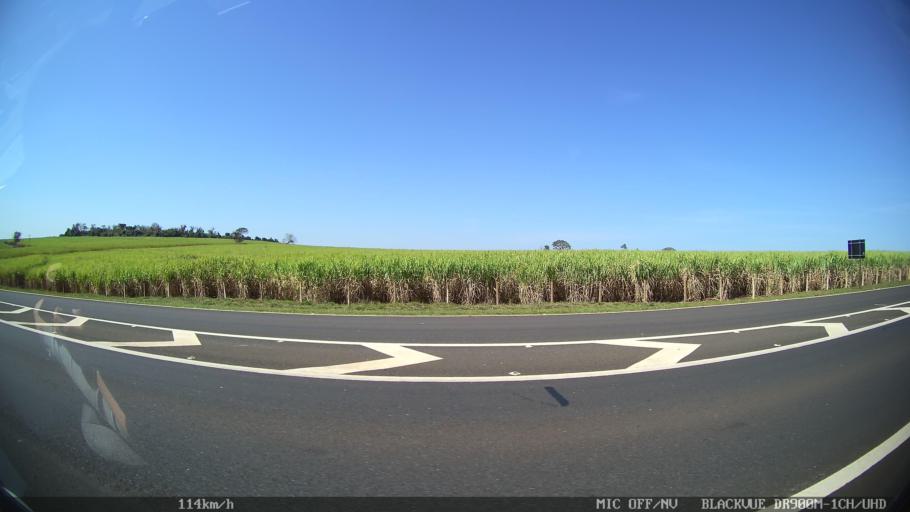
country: BR
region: Sao Paulo
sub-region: Batatais
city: Batatais
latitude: -20.7888
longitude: -47.5582
